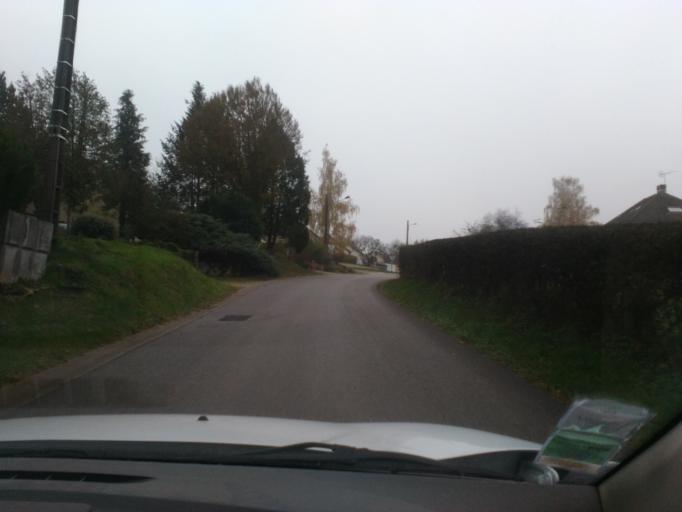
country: FR
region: Lorraine
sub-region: Departement des Vosges
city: Neufchateau
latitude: 48.3590
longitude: 5.7363
